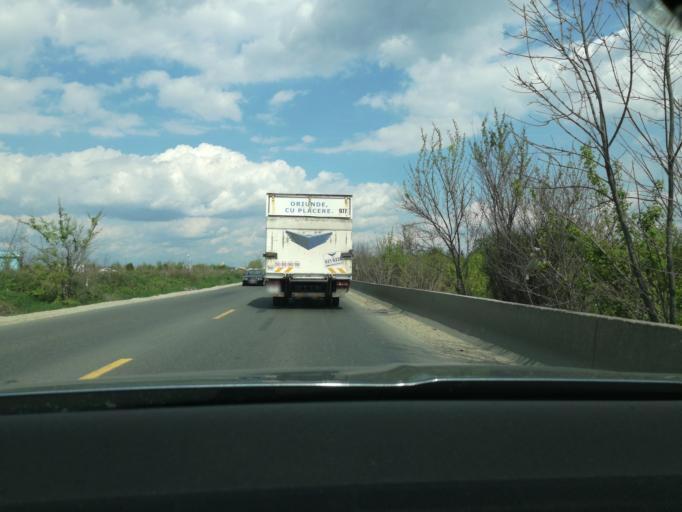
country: RO
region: Ilfov
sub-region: Comuna Chitila
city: Rudeni
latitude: 44.4746
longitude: 25.9647
